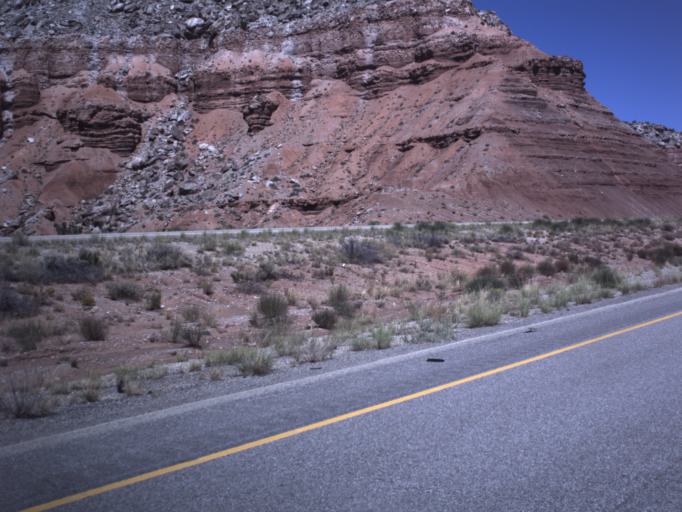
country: US
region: Utah
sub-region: Emery County
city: Ferron
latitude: 38.8284
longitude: -111.1397
